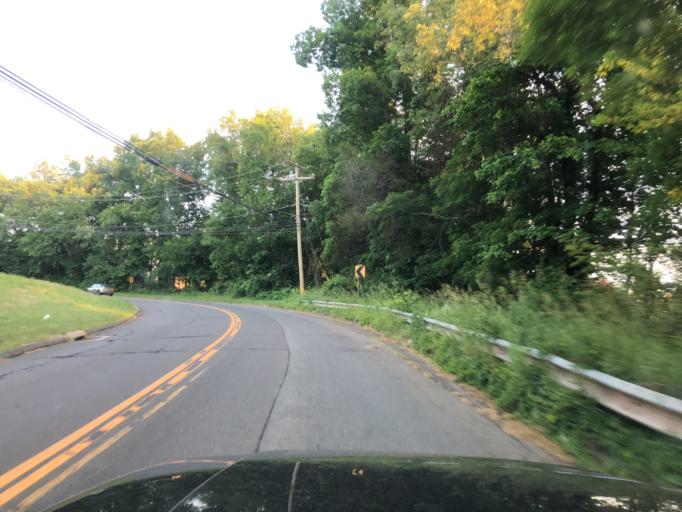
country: US
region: Connecticut
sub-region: Middlesex County
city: Middletown
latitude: 41.5631
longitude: -72.7135
